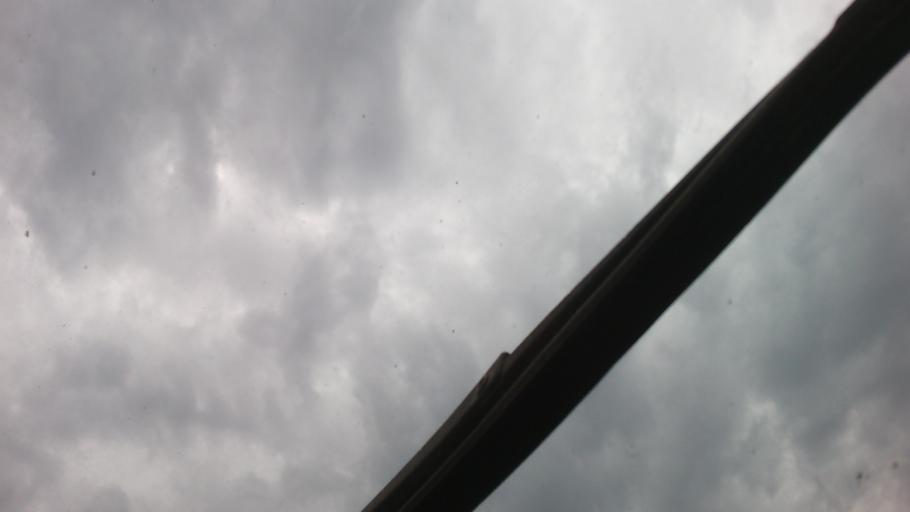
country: BJ
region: Mono
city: Lokossa
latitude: 6.5729
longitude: 1.7891
